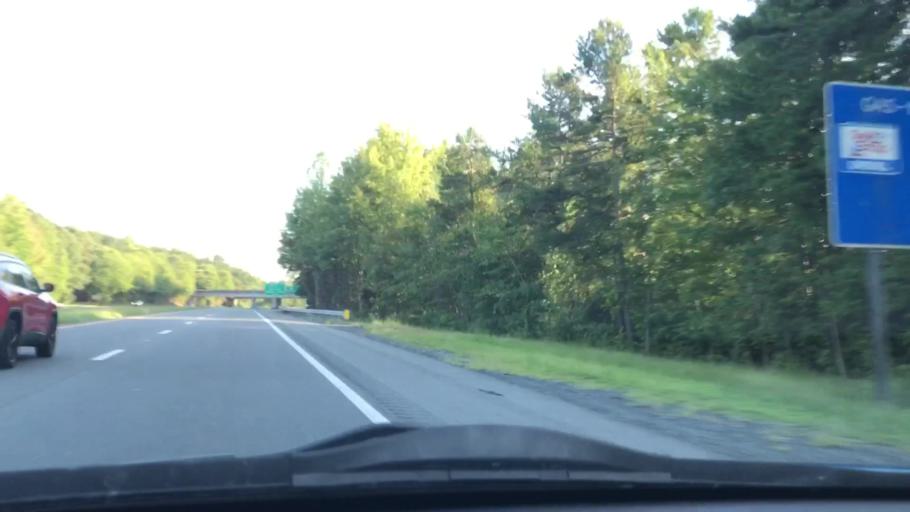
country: US
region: North Carolina
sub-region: Randolph County
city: Randleman
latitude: 35.8154
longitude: -79.8244
